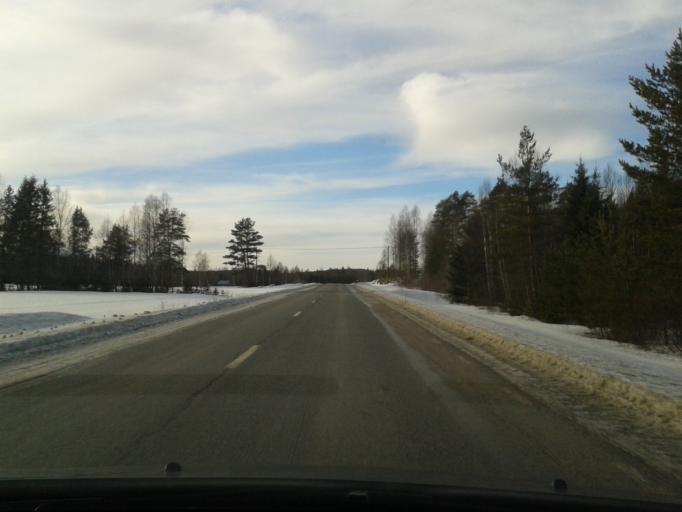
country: SE
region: Vaesternorrland
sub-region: OErnskoeldsviks Kommun
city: Bredbyn
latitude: 63.5273
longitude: 18.0026
